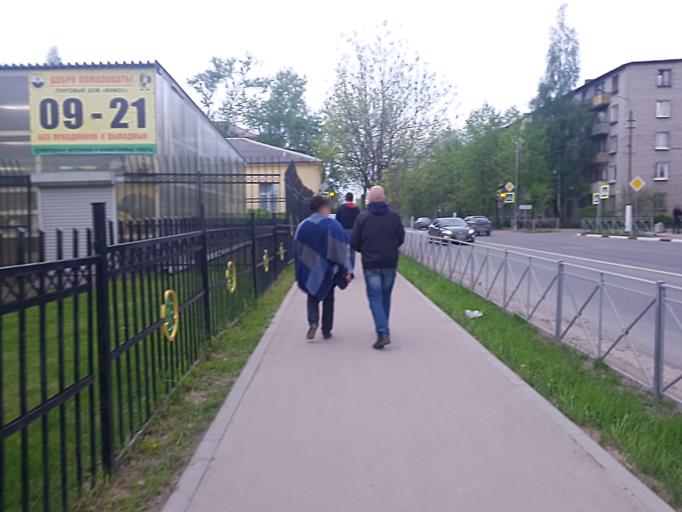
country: RU
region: Leningrad
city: Priozersk
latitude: 61.0344
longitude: 30.1209
